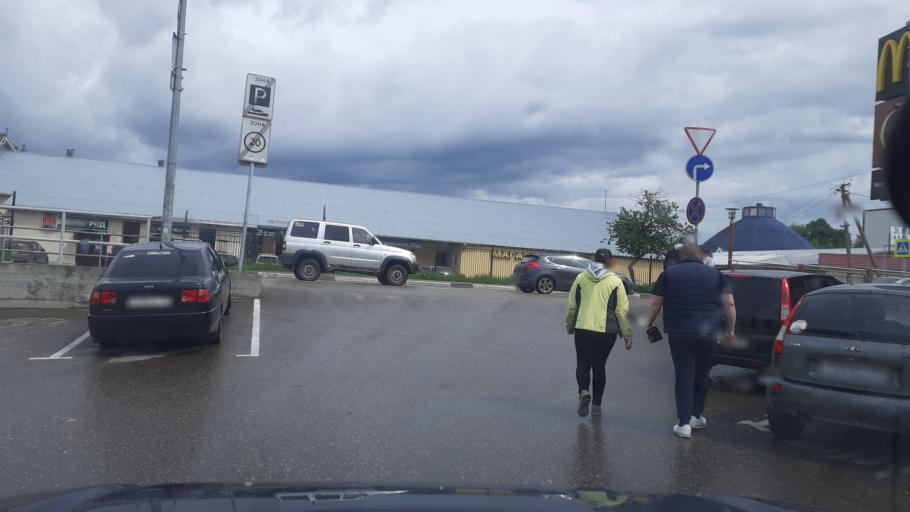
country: RU
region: Moskovskaya
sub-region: Volokolamskiy Rayon
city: Volokolamsk
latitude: 56.0312
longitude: 35.9587
